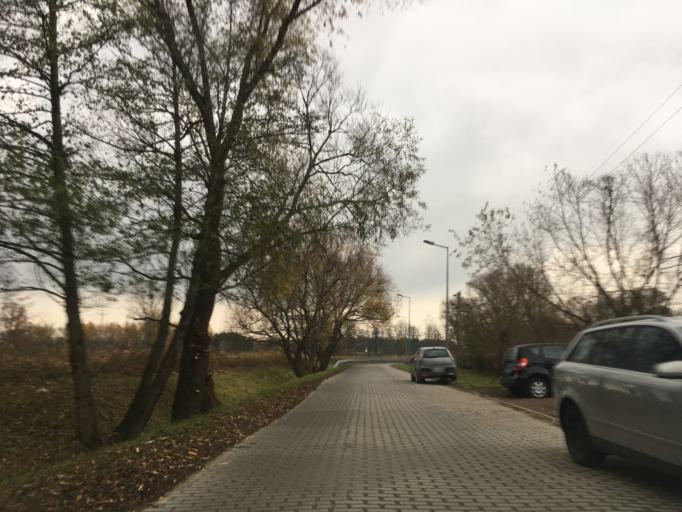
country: PL
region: Masovian Voivodeship
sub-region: Powiat piaseczynski
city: Lesznowola
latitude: 52.0412
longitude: 20.9427
